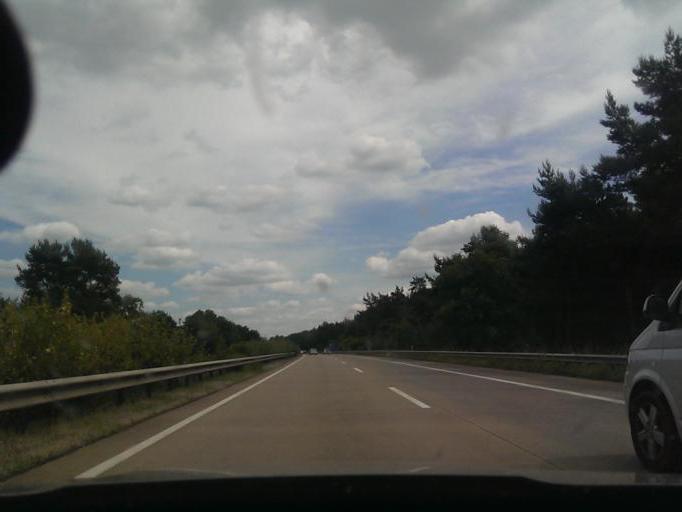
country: DE
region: Lower Saxony
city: Verden
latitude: 52.9431
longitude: 9.2627
